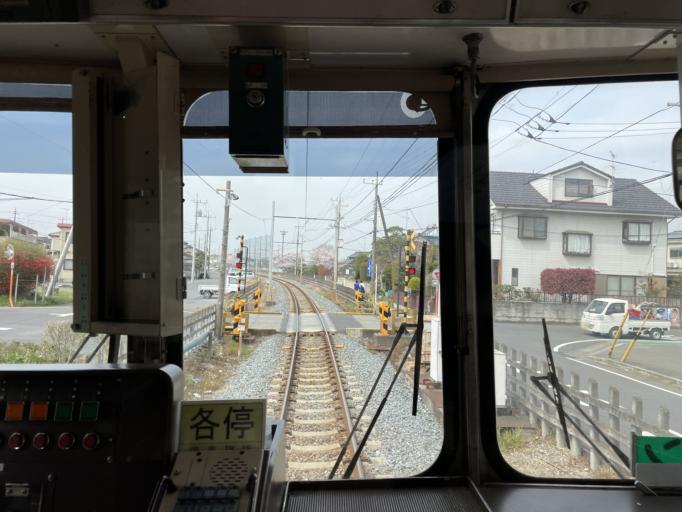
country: JP
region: Saitama
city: Hanyu
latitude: 36.1751
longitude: 139.5306
